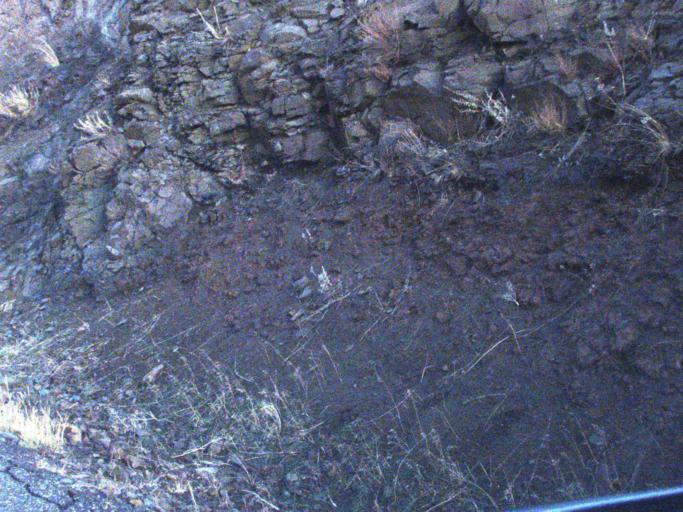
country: US
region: Washington
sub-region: Asotin County
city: Asotin
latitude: 46.0027
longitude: -117.2779
